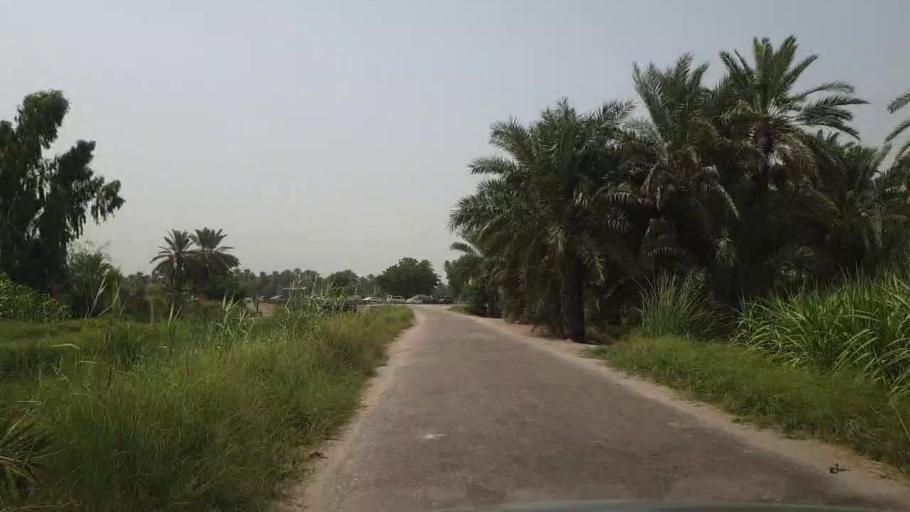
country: PK
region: Sindh
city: Gambat
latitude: 27.3793
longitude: 68.5482
